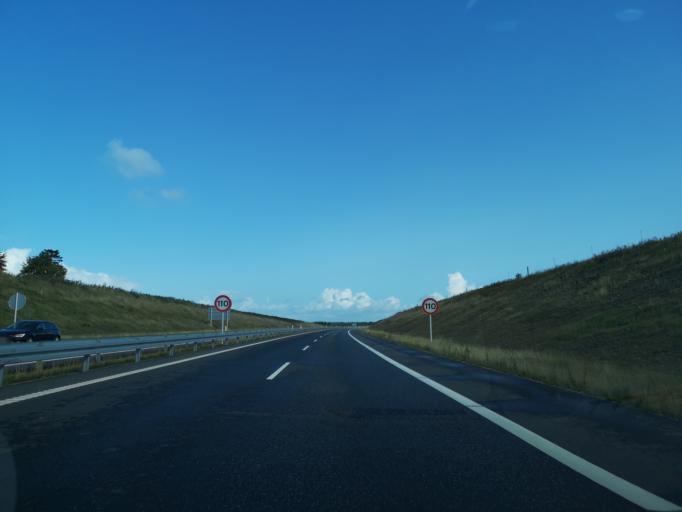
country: DK
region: Central Jutland
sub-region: Herning Kommune
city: Snejbjerg
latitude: 56.1353
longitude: 8.8702
